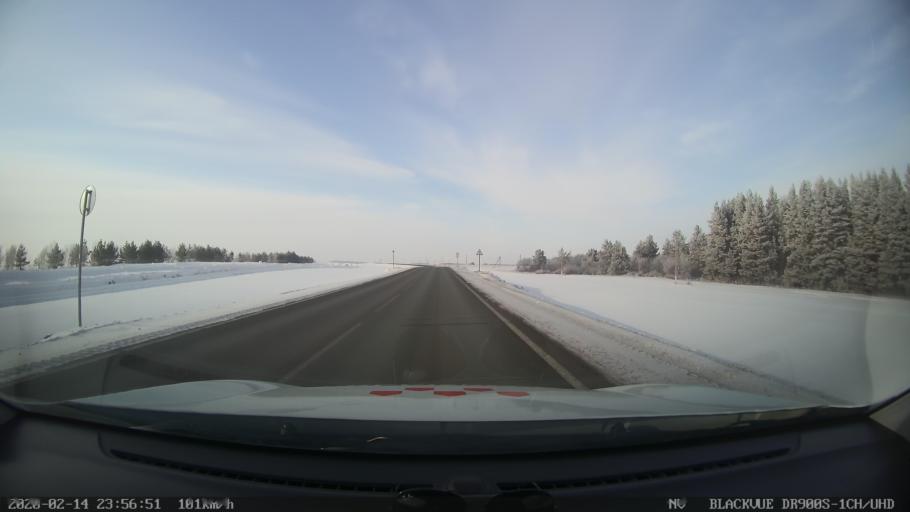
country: RU
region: Tatarstan
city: Kuybyshevskiy Zaton
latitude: 55.3287
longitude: 49.1230
